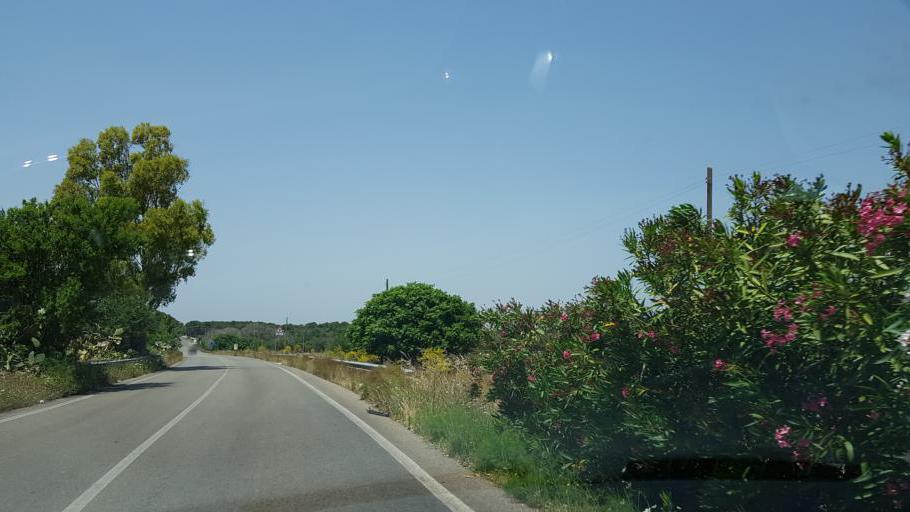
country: IT
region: Apulia
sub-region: Provincia di Lecce
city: Porto Cesareo
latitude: 40.2642
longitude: 17.9167
